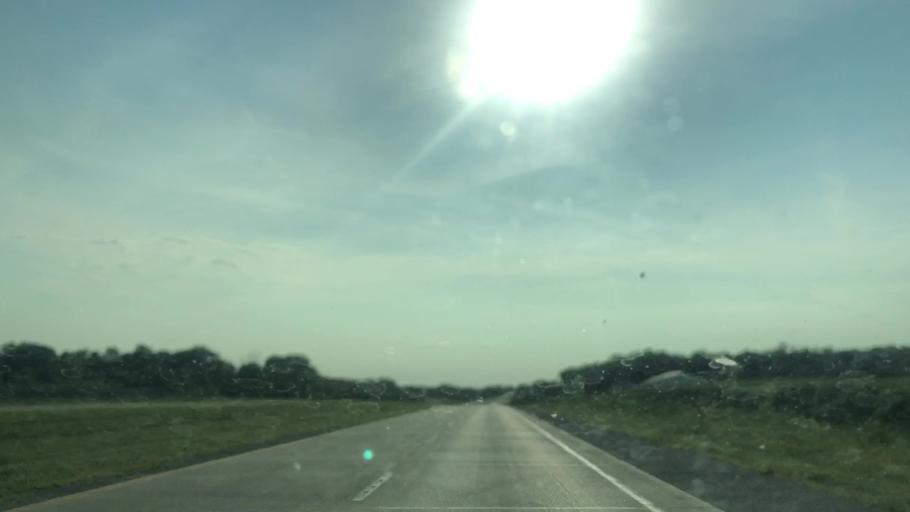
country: US
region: Iowa
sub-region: Story County
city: Nevada
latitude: 42.0080
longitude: -93.3680
